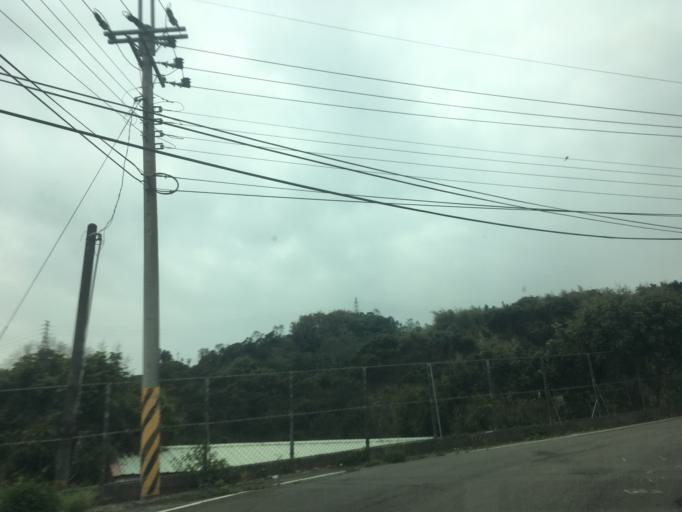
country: TW
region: Taiwan
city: Zhongxing New Village
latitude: 24.0337
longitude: 120.7240
